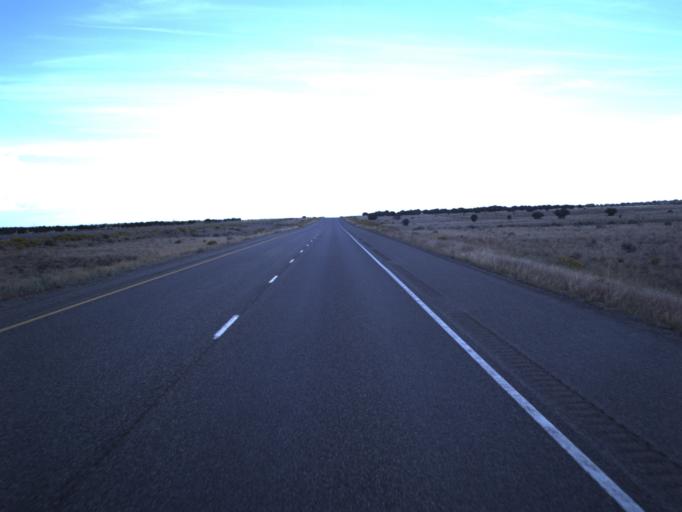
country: US
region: Utah
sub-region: Emery County
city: Castle Dale
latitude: 38.8936
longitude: -110.6213
